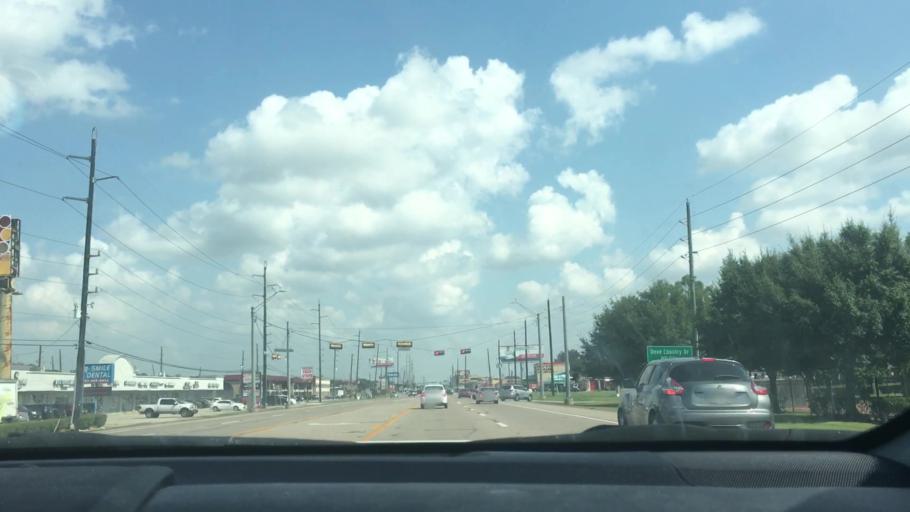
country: US
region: Texas
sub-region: Fort Bend County
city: Stafford
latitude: 29.6074
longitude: -95.5644
